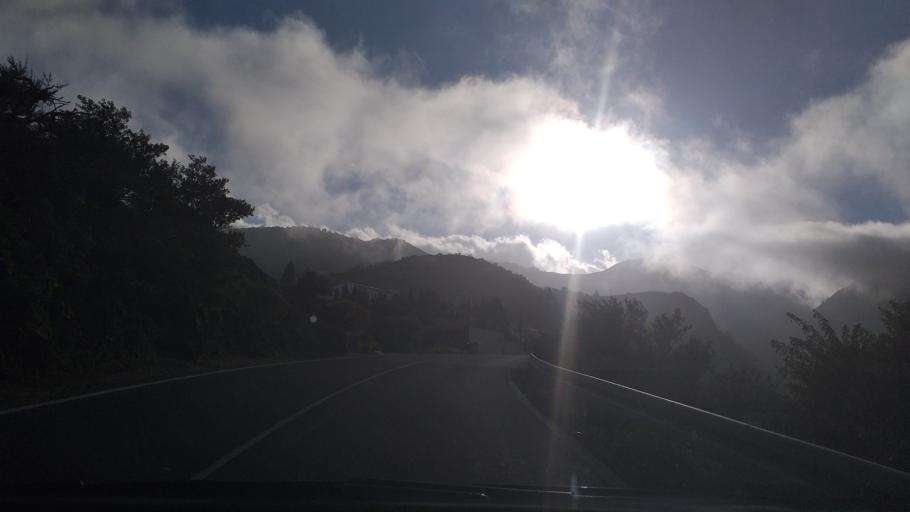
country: ES
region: Canary Islands
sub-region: Provincia de Las Palmas
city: Valsequillo de Gran Canaria
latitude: 27.9570
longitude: -15.5096
